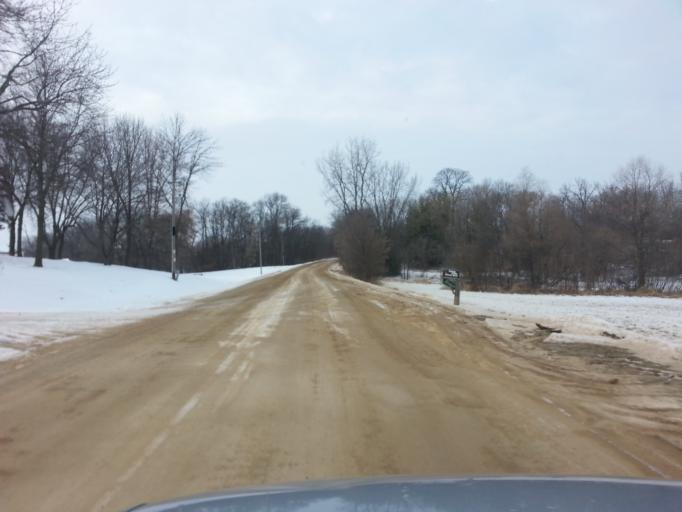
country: US
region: Minnesota
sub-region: Scott County
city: Prior Lake
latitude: 44.7201
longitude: -93.4766
